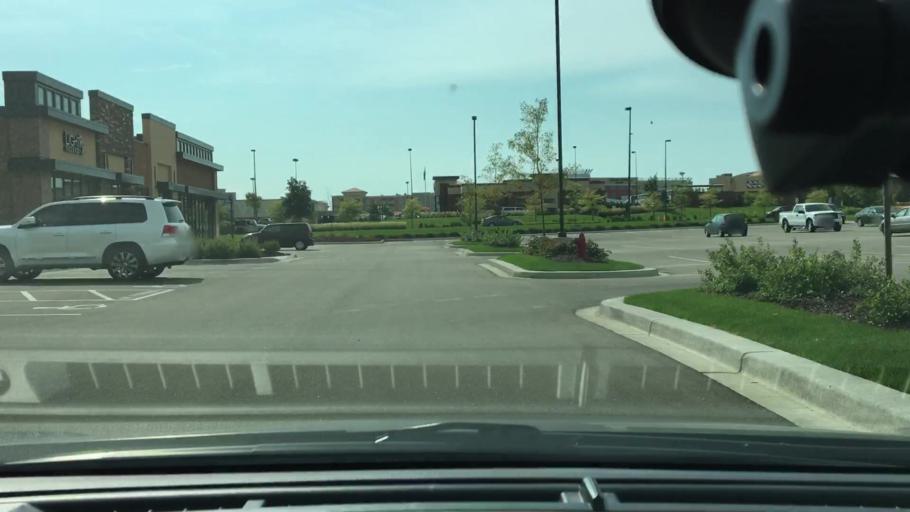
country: US
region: Minnesota
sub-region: Hennepin County
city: Maple Grove
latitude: 45.0958
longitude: -93.4295
